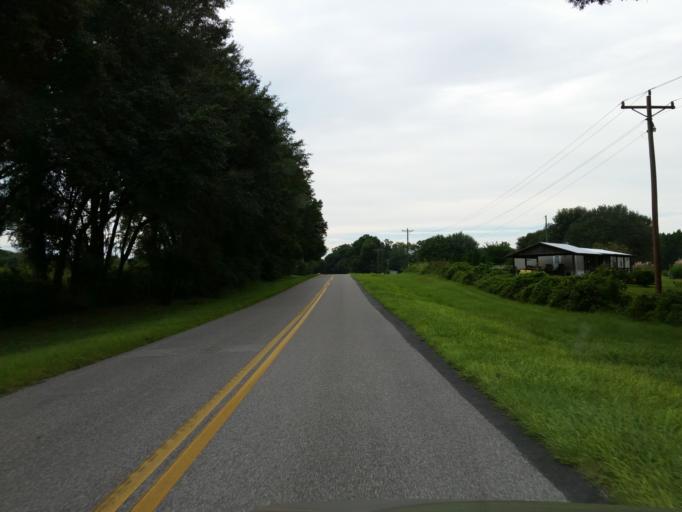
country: US
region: Florida
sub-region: Alachua County
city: High Springs
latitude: 29.9516
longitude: -82.5114
